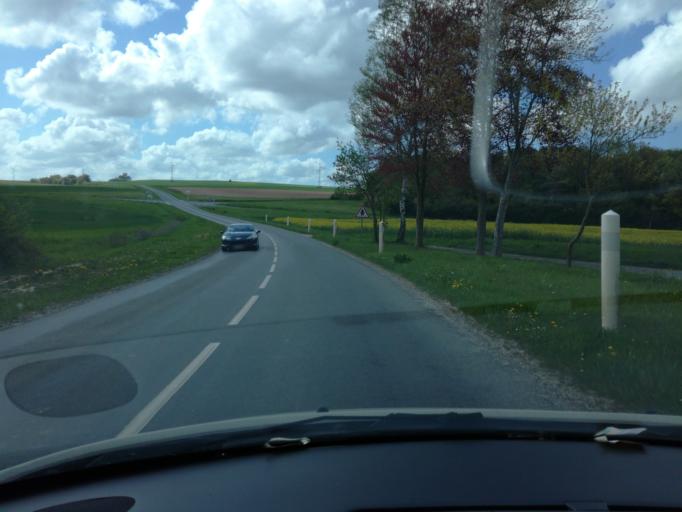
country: FR
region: Picardie
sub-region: Departement de la Somme
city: Quevauvillers
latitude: 49.8860
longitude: 2.0632
